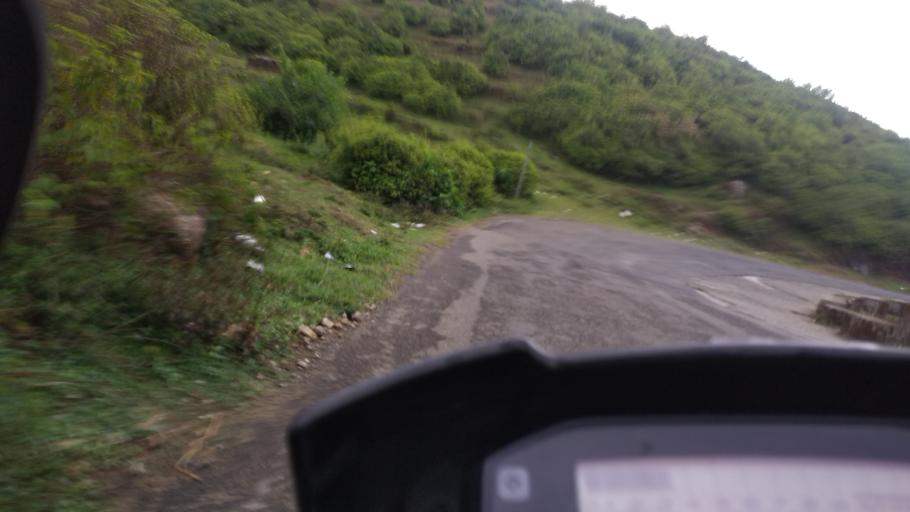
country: IN
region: Kerala
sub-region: Kottayam
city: Erattupetta
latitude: 9.6323
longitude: 76.9443
